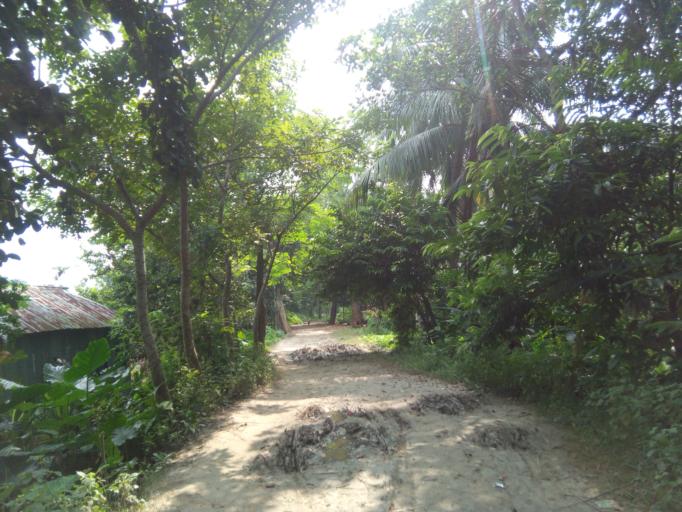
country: BD
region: Khulna
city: Kalia
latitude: 23.0593
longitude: 89.6558
